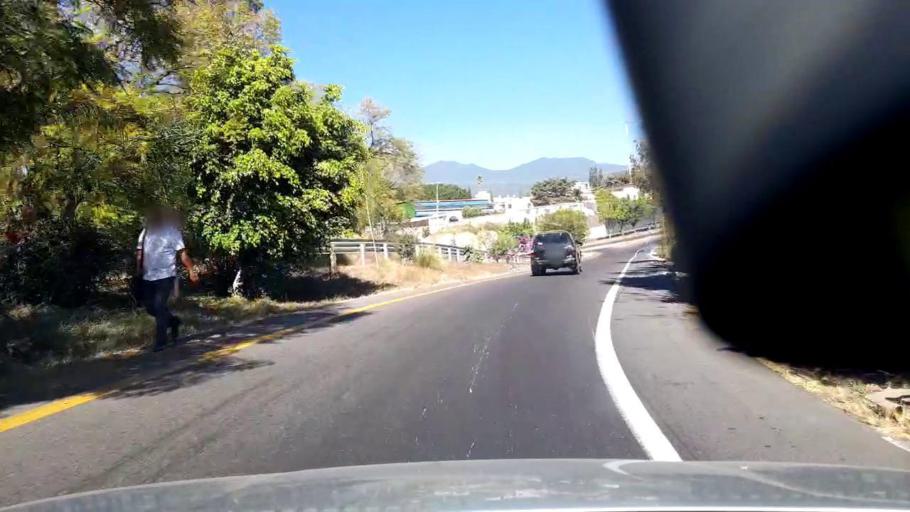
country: MX
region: Morelos
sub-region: Cuernavaca
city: Fraccionamiento Lomas de Ahuatlan
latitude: 18.9603
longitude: -99.2283
